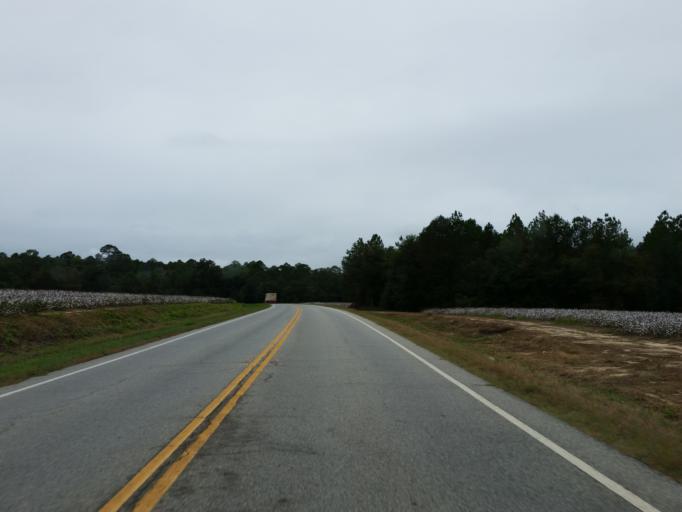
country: US
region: Georgia
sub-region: Cook County
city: Adel
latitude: 31.1299
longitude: -83.3400
